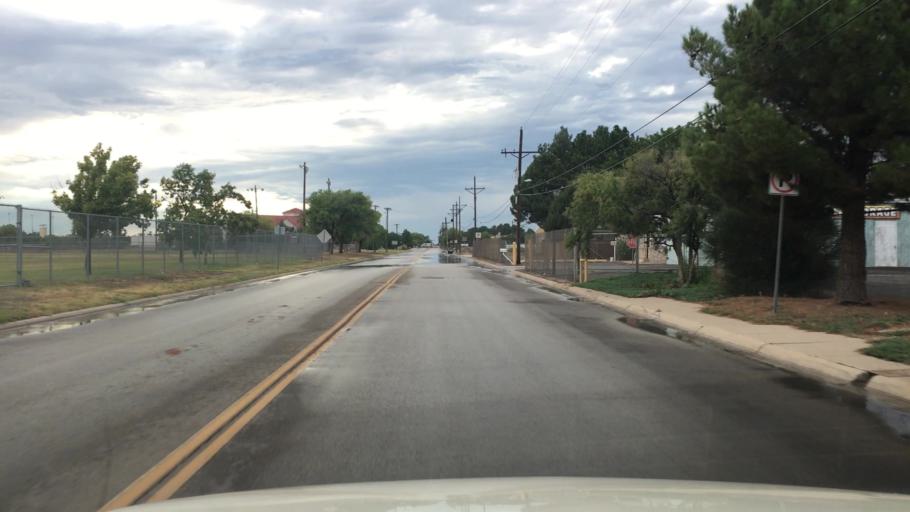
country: US
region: New Mexico
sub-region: Chaves County
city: Roswell
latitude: 33.4160
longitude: -104.5152
